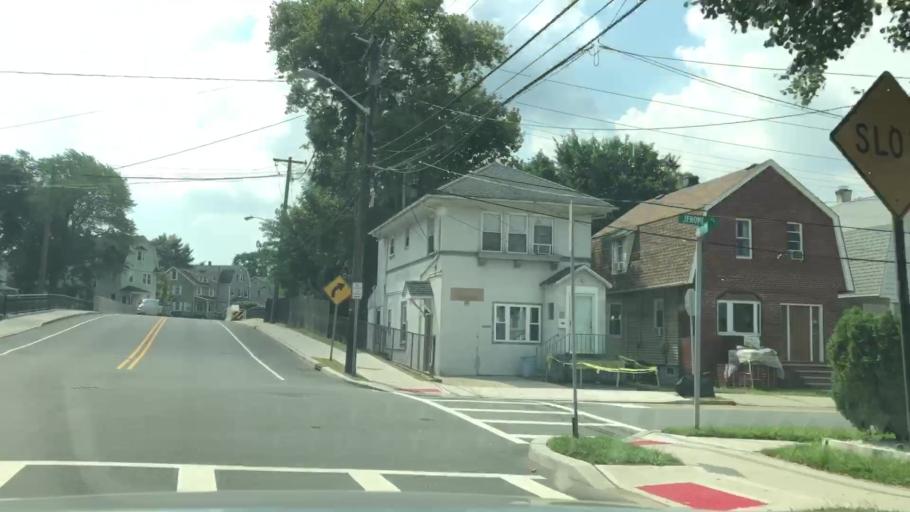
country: US
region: New Jersey
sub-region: Essex County
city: Bloomfield
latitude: 40.7921
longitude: -74.1857
